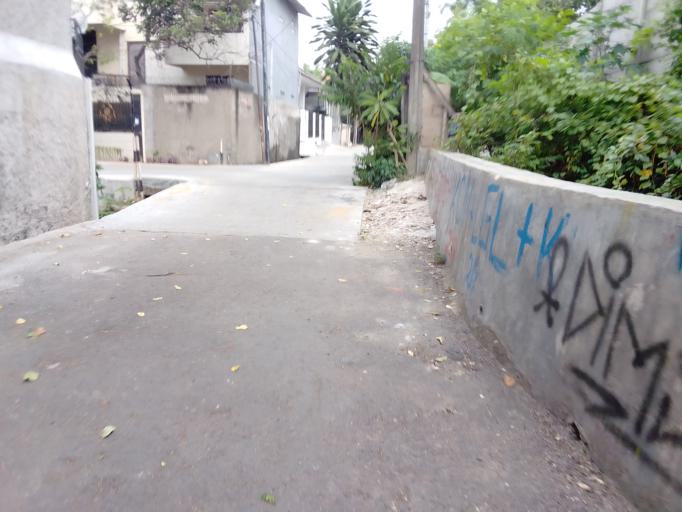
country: ID
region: Jakarta Raya
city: Jakarta
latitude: -6.2004
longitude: 106.8055
